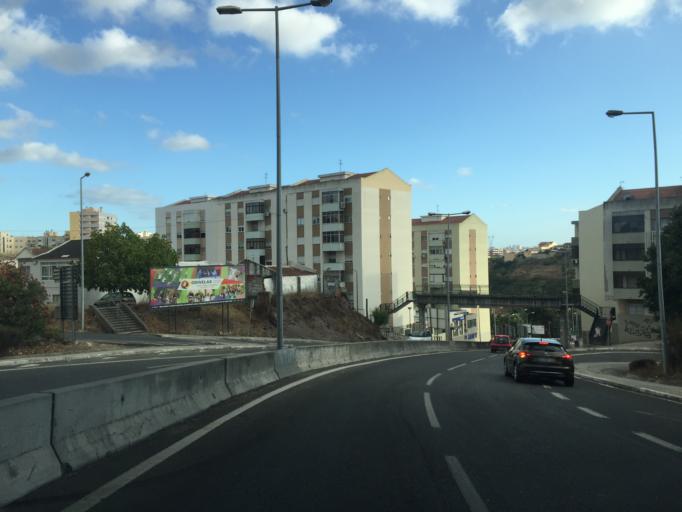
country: PT
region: Lisbon
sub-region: Odivelas
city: Ramada
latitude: 38.8017
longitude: -9.1865
